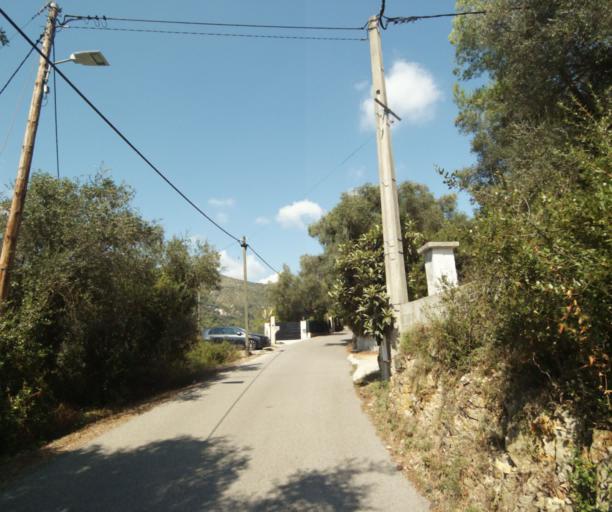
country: FR
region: Provence-Alpes-Cote d'Azur
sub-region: Departement des Alpes-Maritimes
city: Cantaron
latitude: 43.7606
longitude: 7.3237
